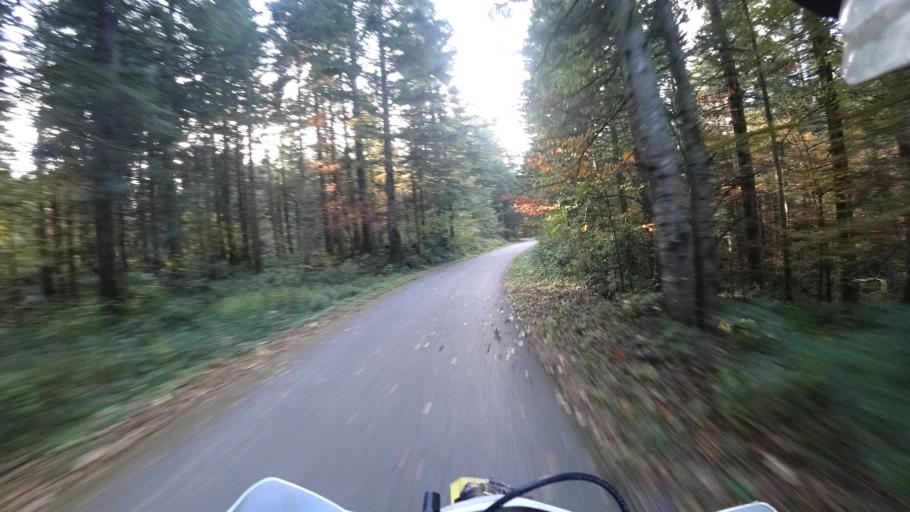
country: HR
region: Karlovacka
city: Plaski
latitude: 44.9828
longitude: 15.4057
